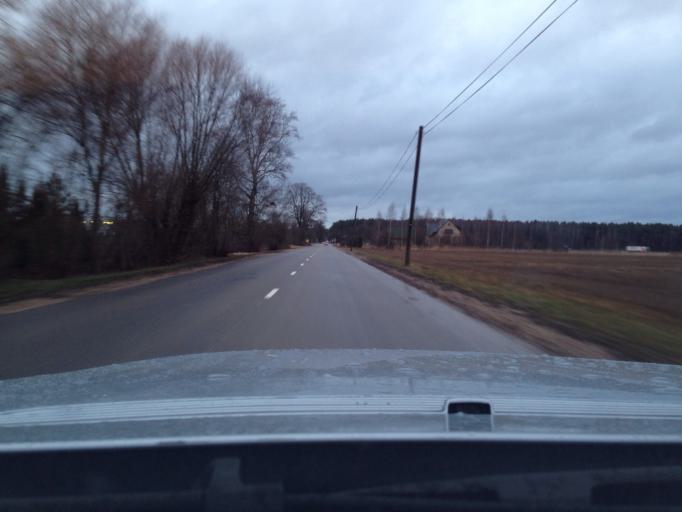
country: LV
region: Marupe
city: Marupe
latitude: 56.8798
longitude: 23.9801
